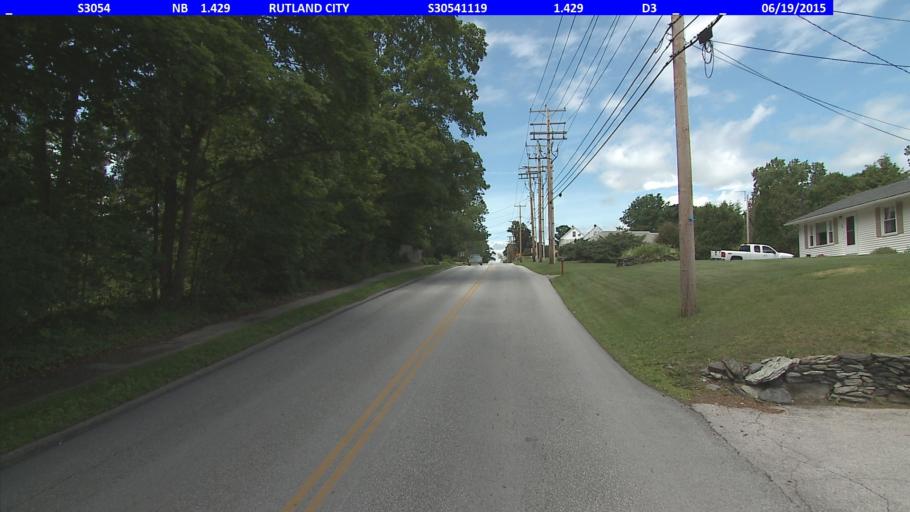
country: US
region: Vermont
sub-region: Rutland County
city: Rutland
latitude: 43.6118
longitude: -72.9566
